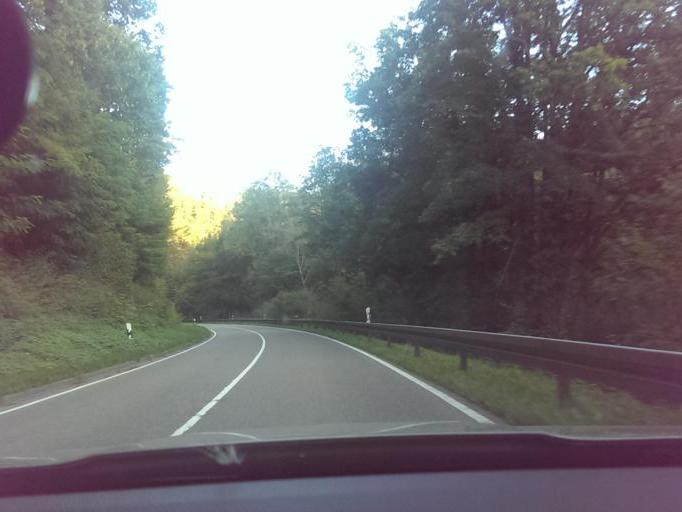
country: DE
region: Baden-Wuerttemberg
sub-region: Karlsruhe Region
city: Unterreichenbach
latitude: 48.8437
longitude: 8.7439
